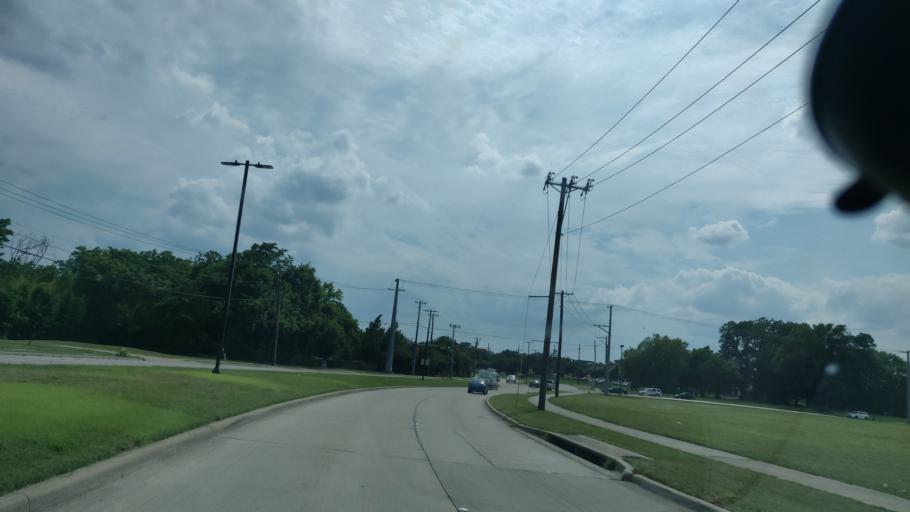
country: US
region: Texas
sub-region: Dallas County
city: Garland
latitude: 32.9359
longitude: -96.6053
